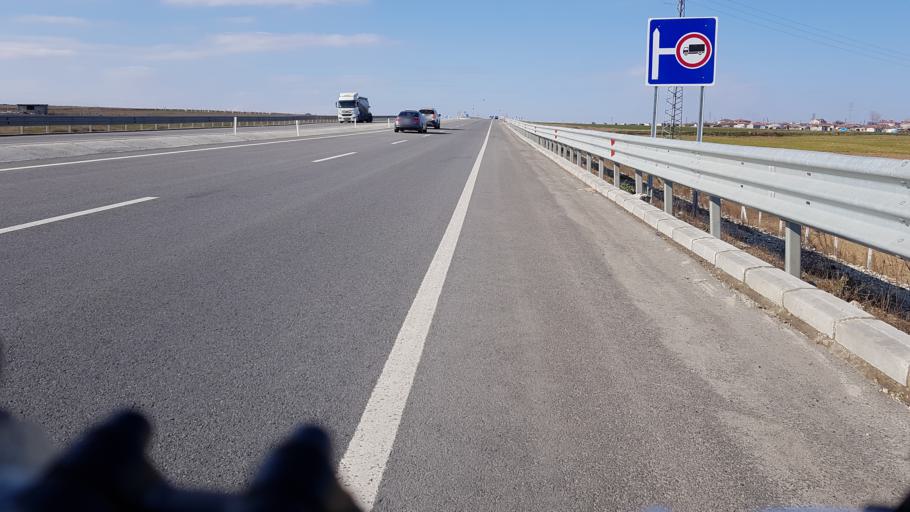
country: TR
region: Tekirdag
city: Saray
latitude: 41.4269
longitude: 27.9118
